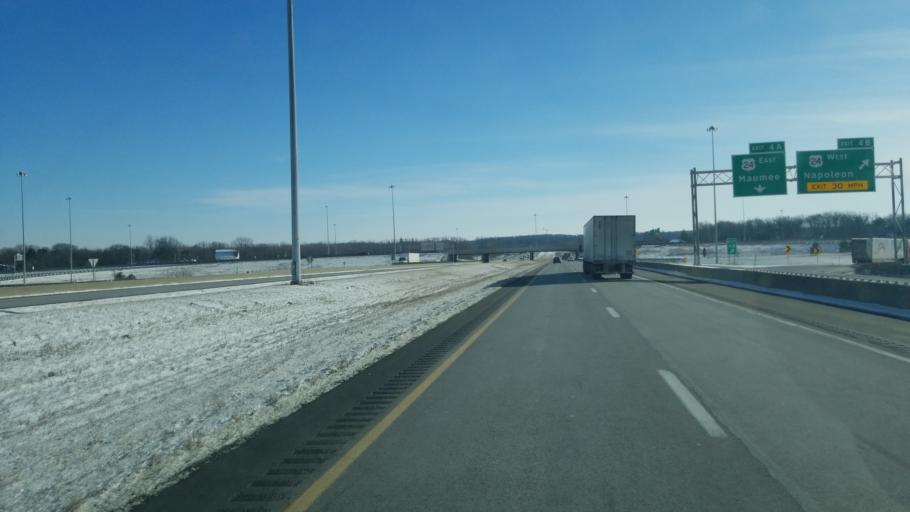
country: US
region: Ohio
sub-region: Lucas County
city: Maumee
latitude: 41.5569
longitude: -83.6873
